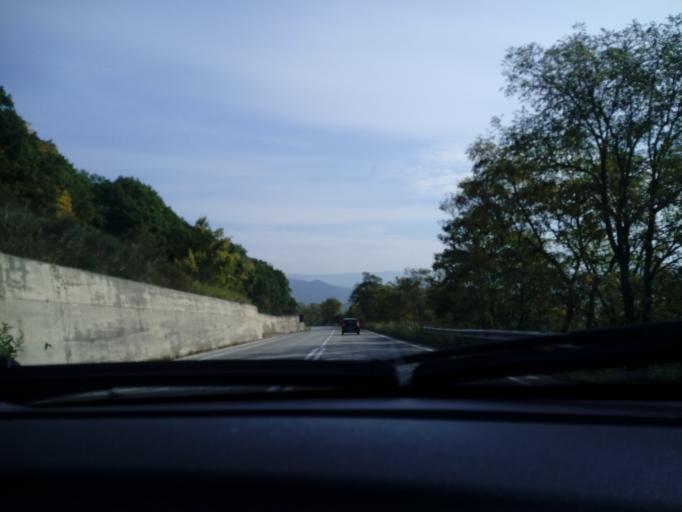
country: IT
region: Molise
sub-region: Provincia di Campobasso
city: Riccia
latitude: 41.5242
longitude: 14.8627
